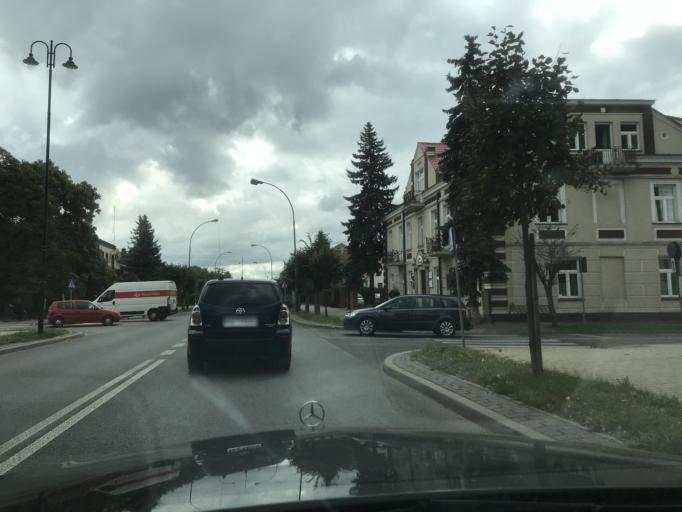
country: PL
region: Lublin Voivodeship
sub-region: Powiat janowski
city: Janow Lubelski
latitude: 50.7023
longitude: 22.4184
